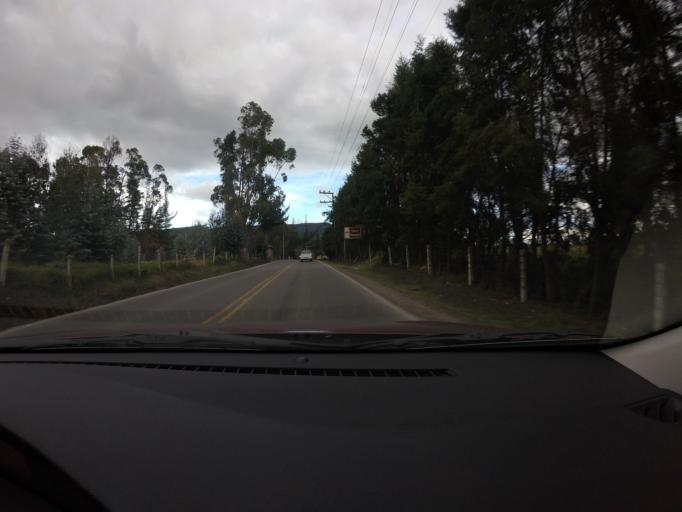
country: CO
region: Cundinamarca
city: Sopo
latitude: 4.9318
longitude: -73.9530
